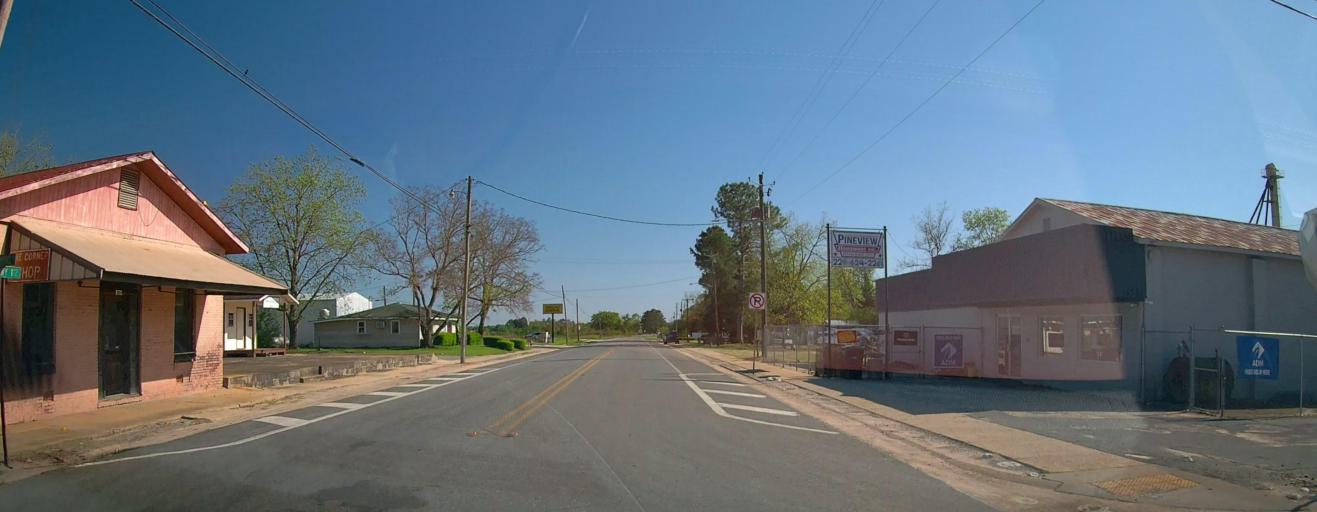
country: US
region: Georgia
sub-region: Wilcox County
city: Rochelle
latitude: 32.1103
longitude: -83.5011
